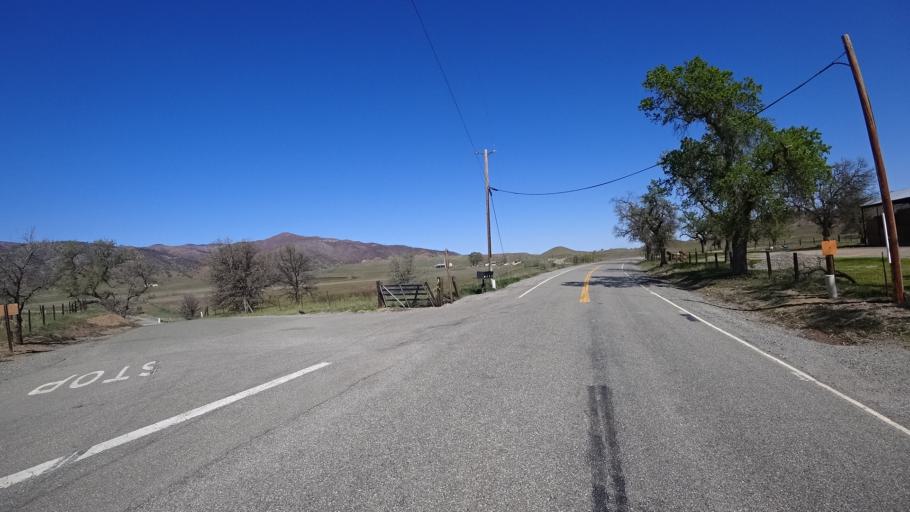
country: US
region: California
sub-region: Tehama County
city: Rancho Tehama Reserve
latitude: 39.6990
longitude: -122.5502
